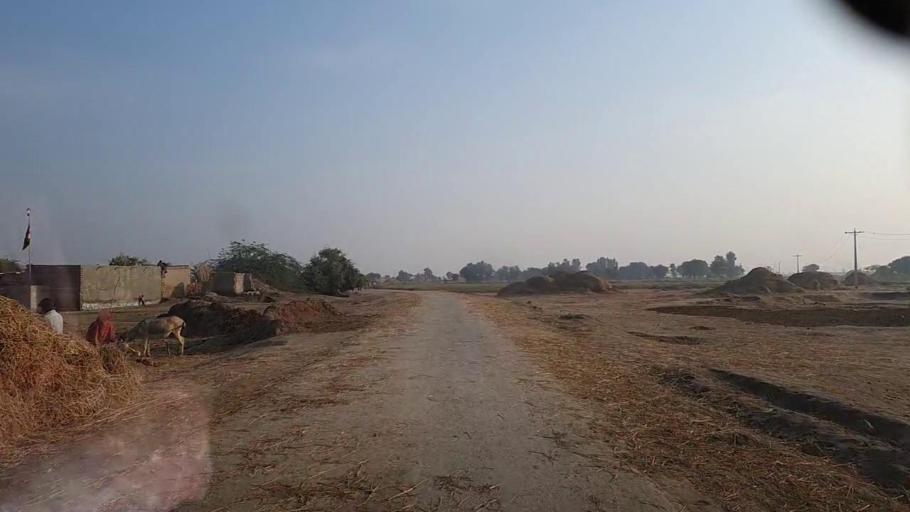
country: PK
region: Sindh
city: Jacobabad
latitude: 28.2356
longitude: 68.4848
